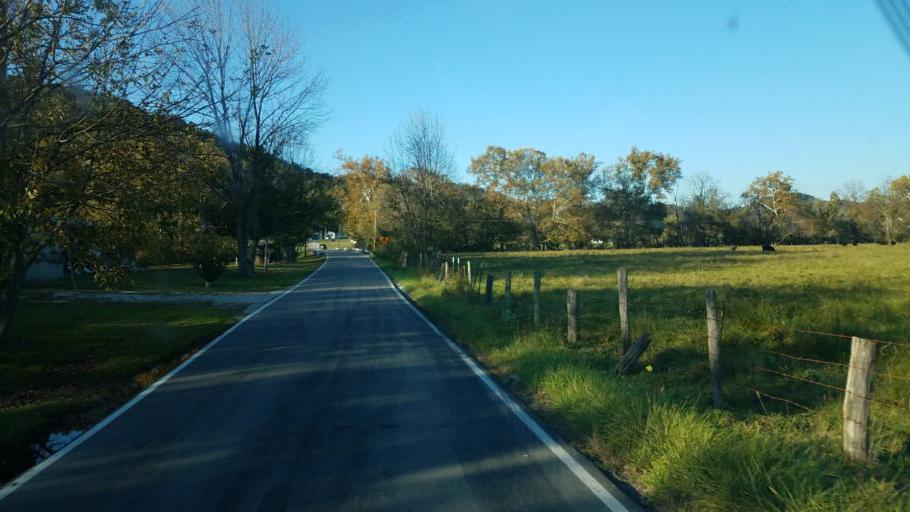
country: US
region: Kentucky
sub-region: Lewis County
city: Vanceburg
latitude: 38.5704
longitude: -83.4329
